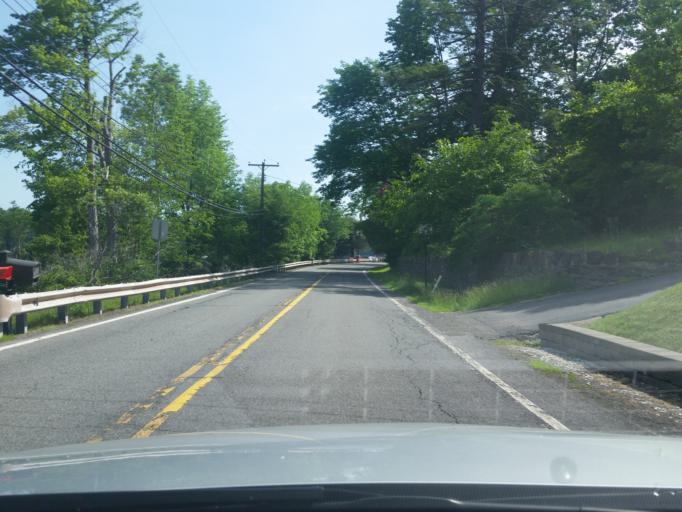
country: US
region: Pennsylvania
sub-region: Luzerne County
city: Harveys Lake
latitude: 41.3722
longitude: -76.0376
